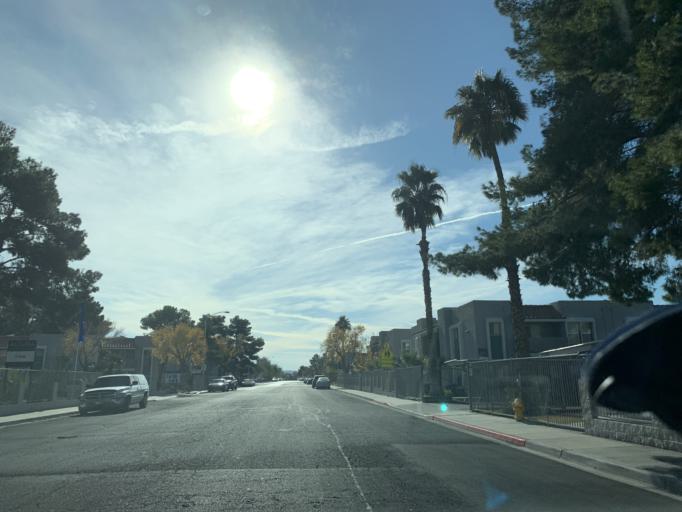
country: US
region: Nevada
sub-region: Clark County
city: Spring Valley
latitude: 36.0982
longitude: -115.2209
